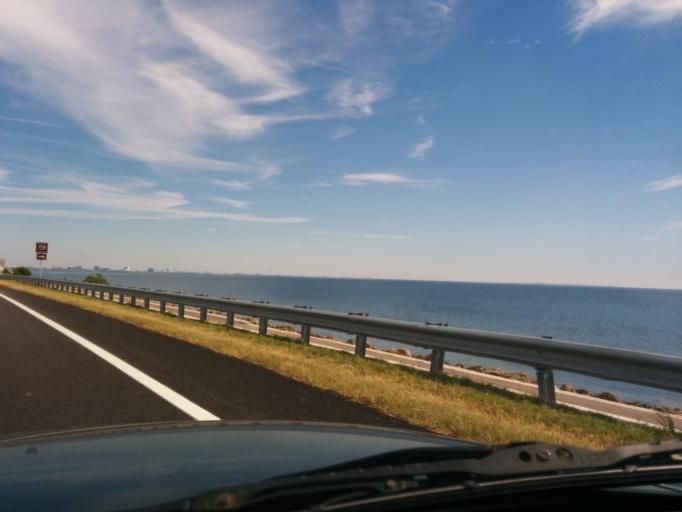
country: US
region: Florida
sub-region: Pinellas County
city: Safety Harbor
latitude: 27.9686
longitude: -82.6351
